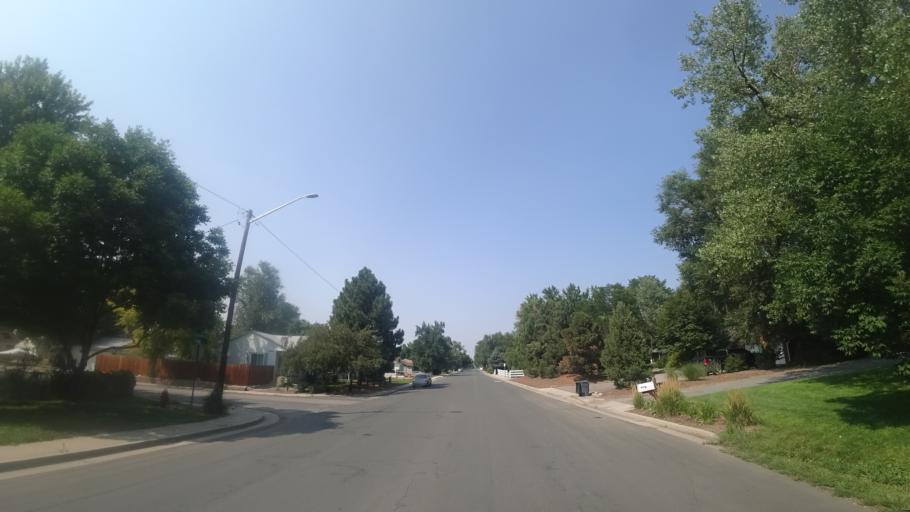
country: US
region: Colorado
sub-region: Arapahoe County
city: Englewood
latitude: 39.6311
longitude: -104.9785
